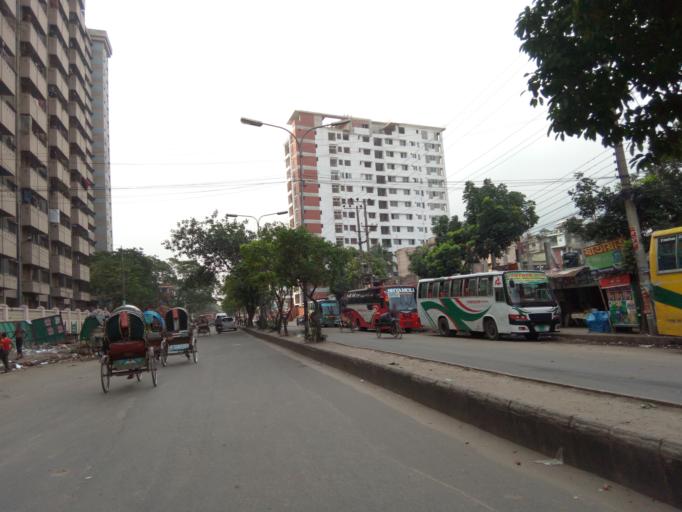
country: BD
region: Dhaka
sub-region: Dhaka
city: Dhaka
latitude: 23.7176
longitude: 90.4292
